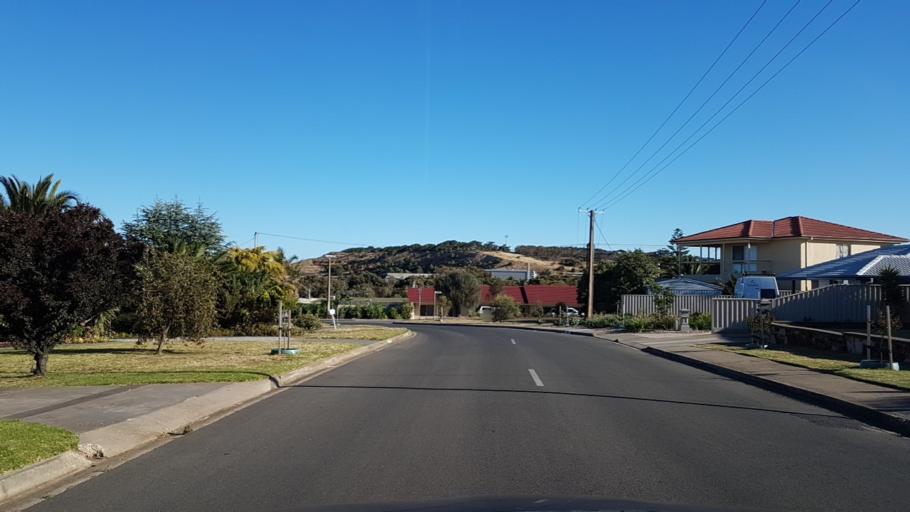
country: AU
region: South Australia
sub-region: Adelaide
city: Port Noarlunga
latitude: -35.1299
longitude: 138.4732
